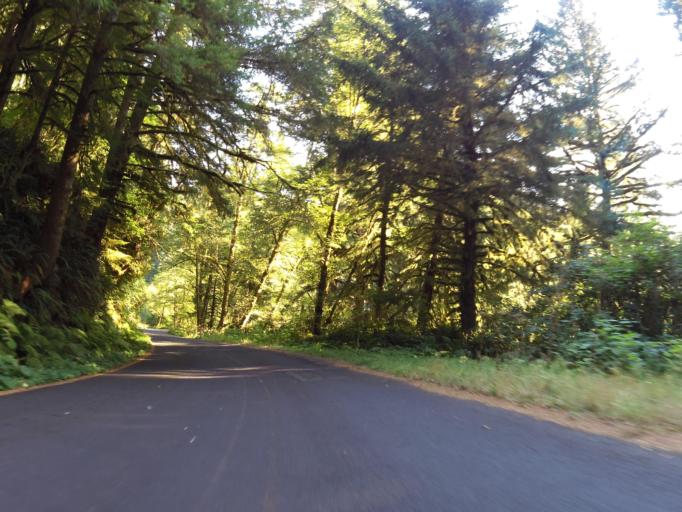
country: US
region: Oregon
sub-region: Lincoln County
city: Rose Lodge
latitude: 45.0376
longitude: -123.9123
